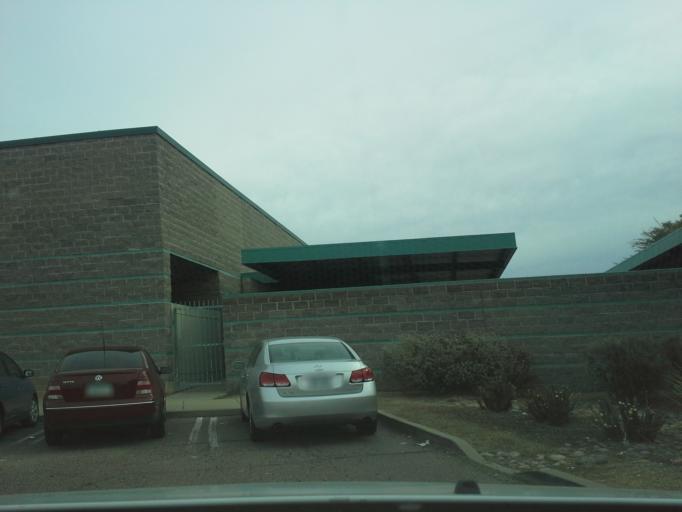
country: US
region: Arizona
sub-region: Maricopa County
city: Paradise Valley
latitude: 33.6255
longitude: -112.0196
